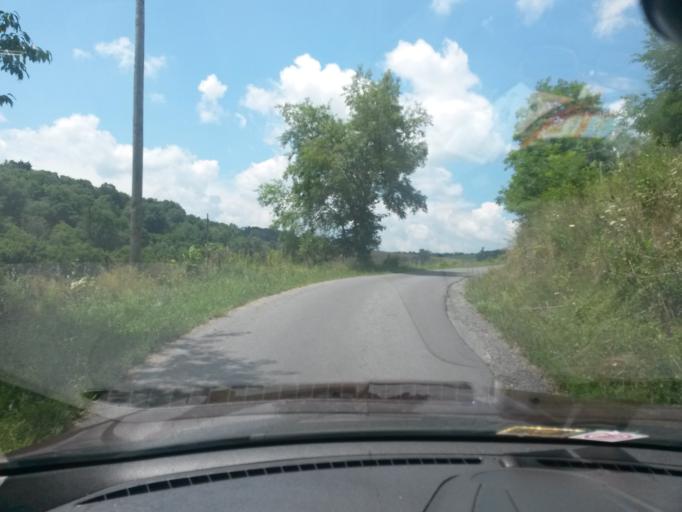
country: US
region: West Virginia
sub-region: Monroe County
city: Union
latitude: 37.5698
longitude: -80.4938
